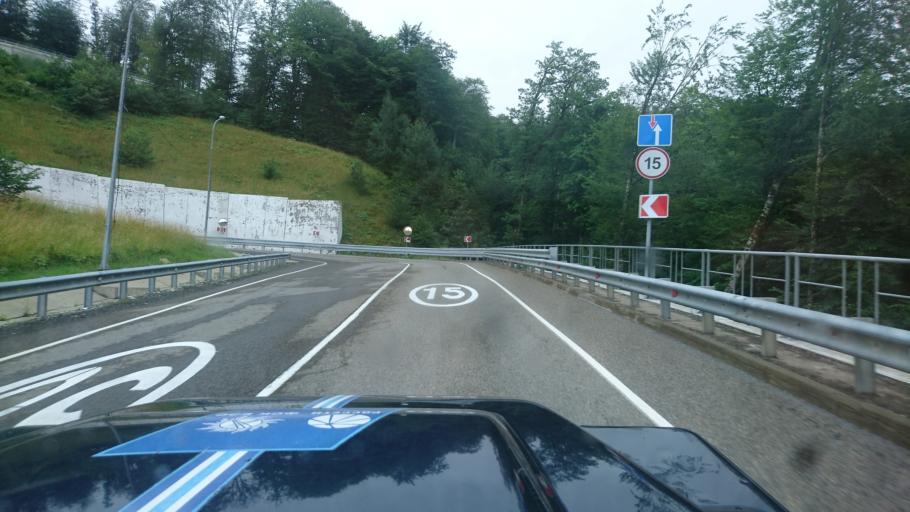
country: RU
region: Krasnodarskiy
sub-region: Sochi City
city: Krasnaya Polyana
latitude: 43.6626
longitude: 40.3108
